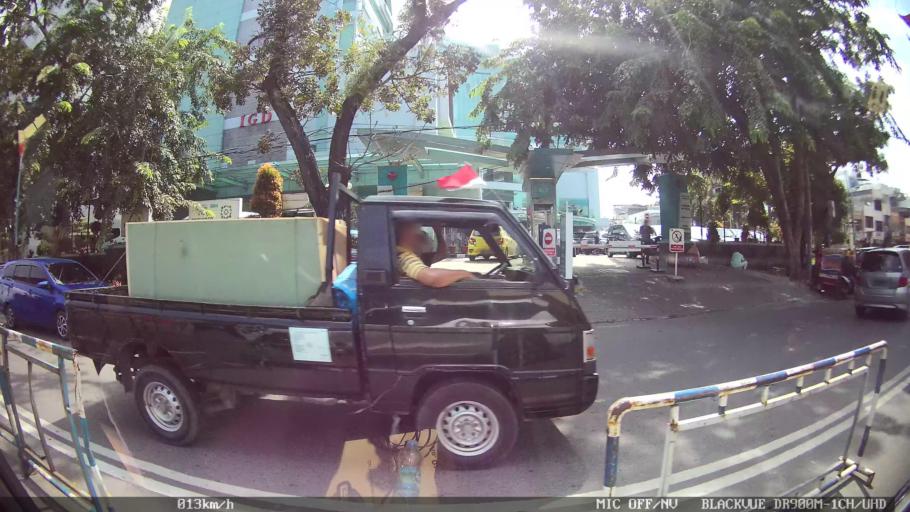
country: ID
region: North Sumatra
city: Medan
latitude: 3.5902
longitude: 98.6813
